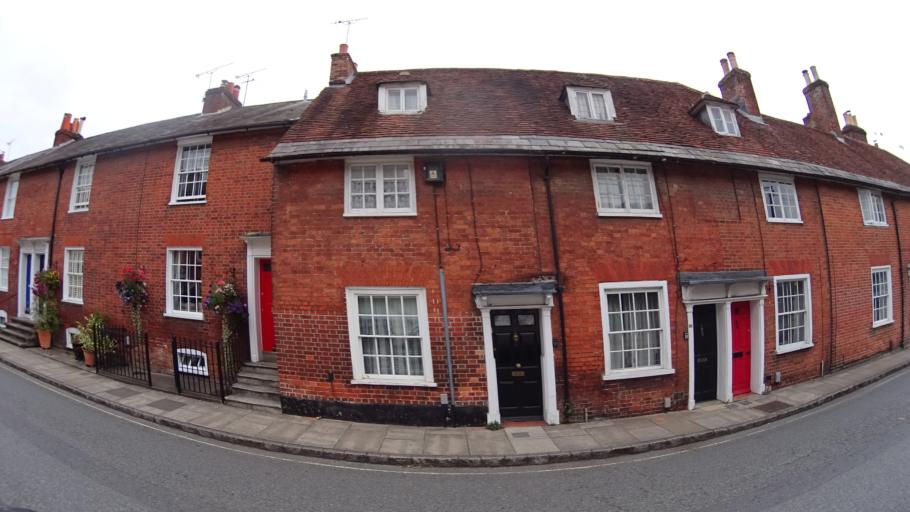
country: GB
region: England
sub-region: Hampshire
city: Romsey
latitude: 50.9880
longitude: -1.4958
